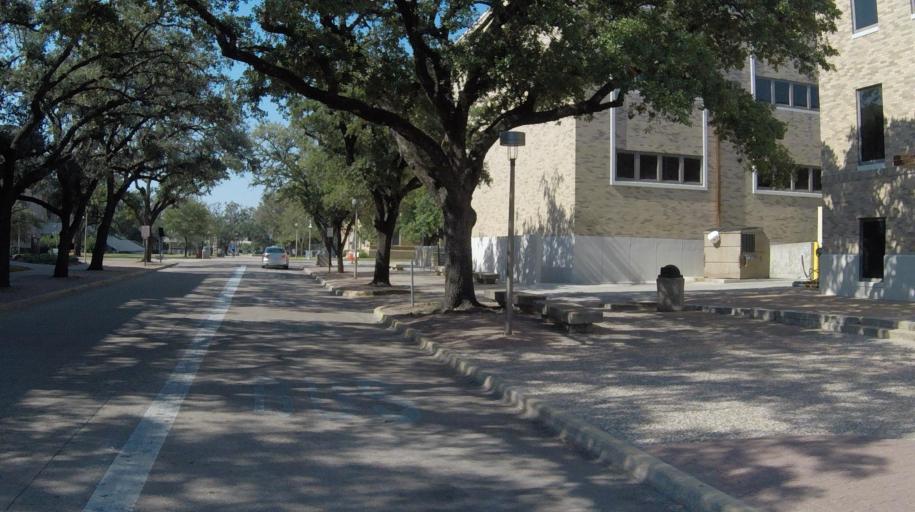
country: US
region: Texas
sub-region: Brazos County
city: College Station
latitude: 30.6146
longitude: -96.3394
